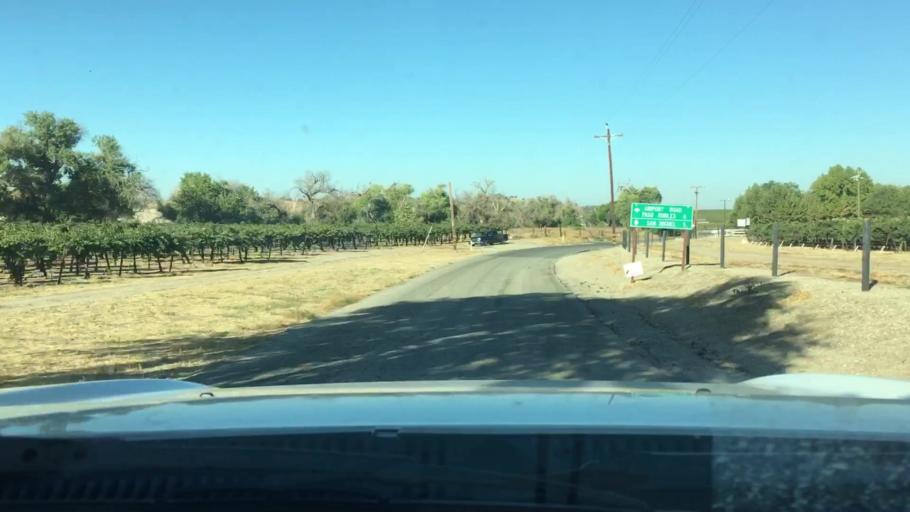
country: US
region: California
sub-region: San Luis Obispo County
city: San Miguel
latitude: 35.7179
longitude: -120.6390
